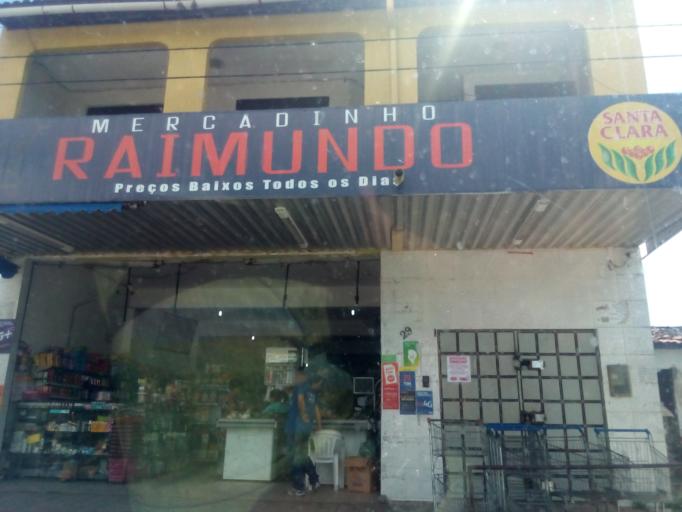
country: BR
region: Rio Grande do Norte
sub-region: Natal
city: Natal
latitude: -5.8255
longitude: -35.2389
